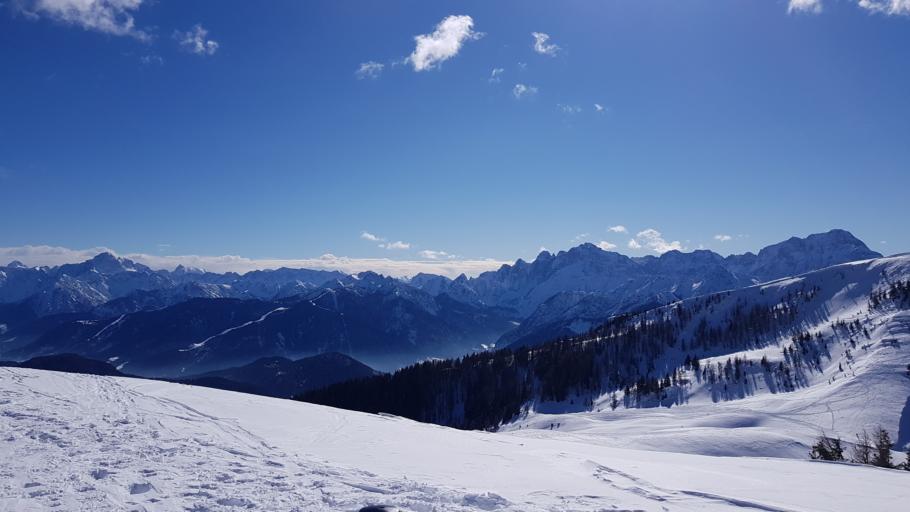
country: IT
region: Friuli Venezia Giulia
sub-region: Provincia di Udine
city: Malborghetto
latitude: 46.5569
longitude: 13.4450
